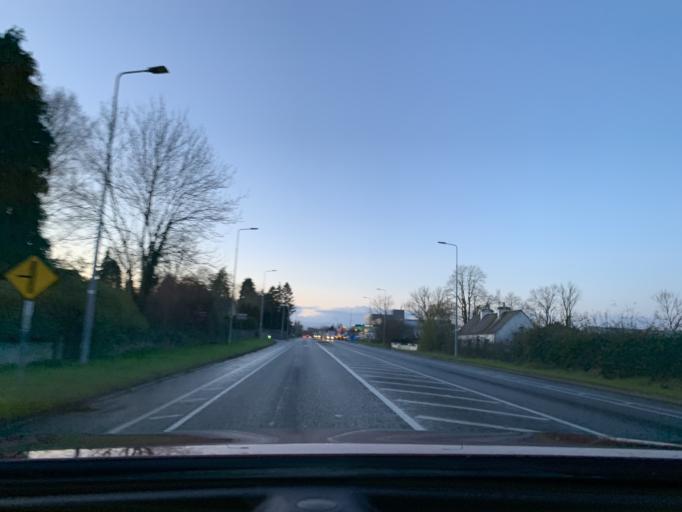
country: IE
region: Connaught
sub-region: County Leitrim
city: Carrick-on-Shannon
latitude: 53.9427
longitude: -8.0690
